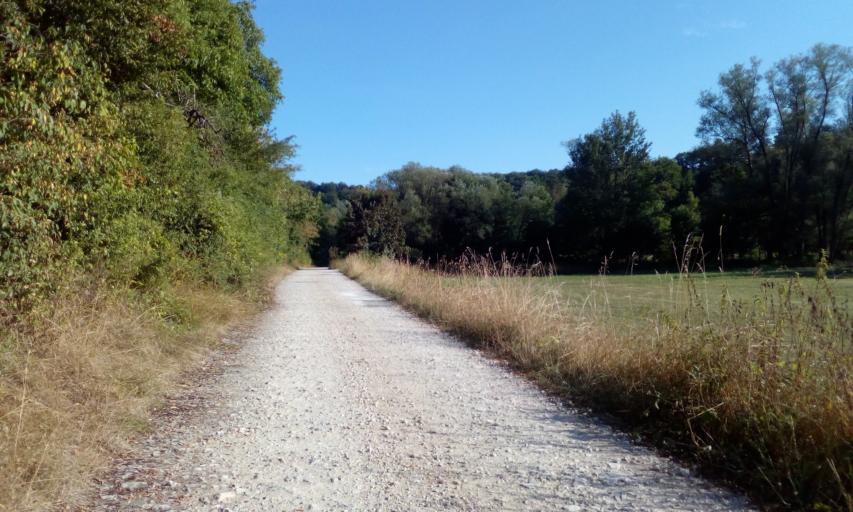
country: FR
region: Lorraine
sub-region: Departement de Meurthe-et-Moselle
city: Pagny-sur-Moselle
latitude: 48.9680
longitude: 5.8866
